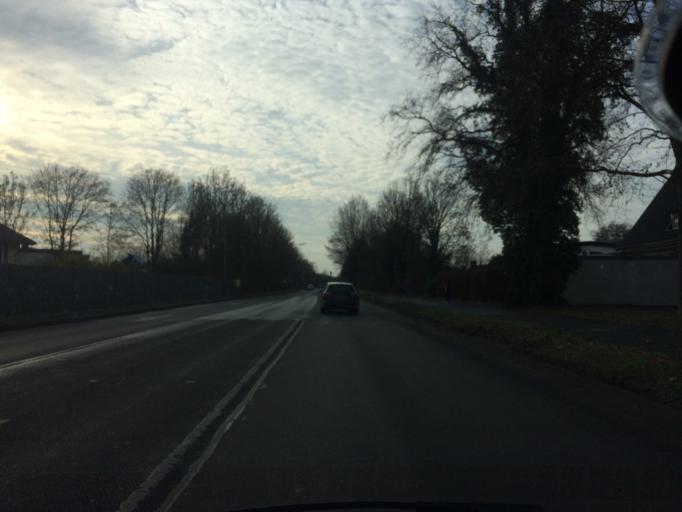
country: DE
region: North Rhine-Westphalia
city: Dorsten
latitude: 51.6510
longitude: 6.9590
